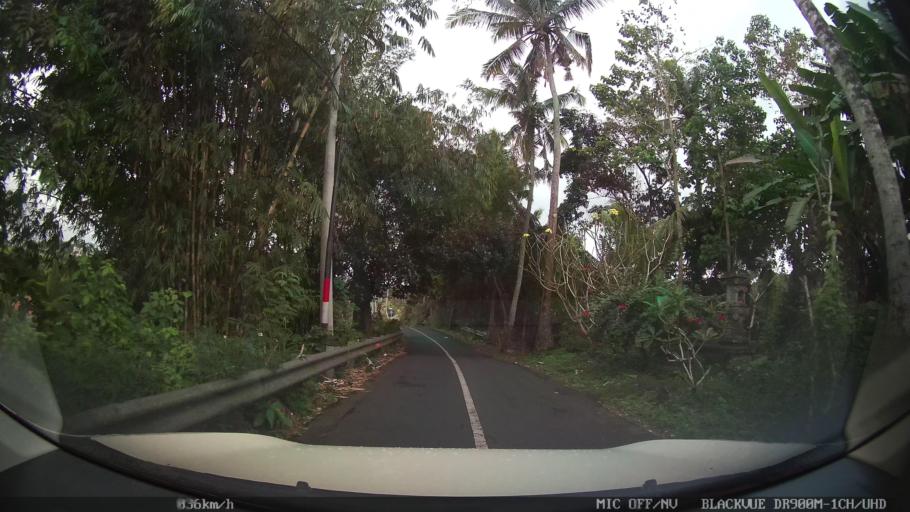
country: ID
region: Bali
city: Banjar Cemenggon
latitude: -8.5338
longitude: 115.1926
